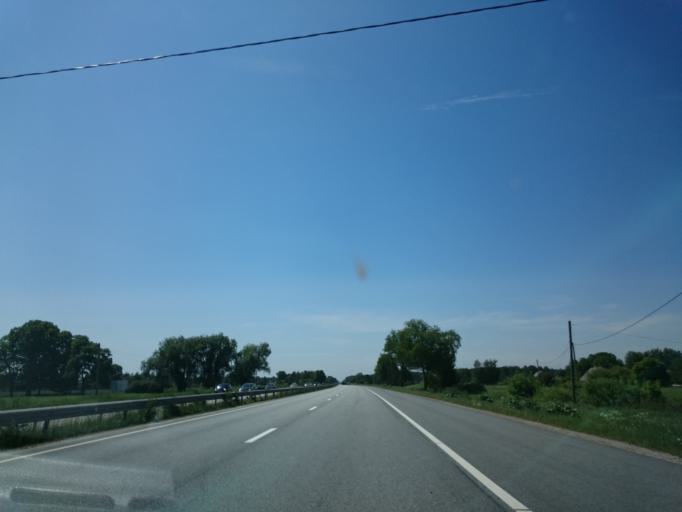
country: LV
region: Olaine
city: Olaine
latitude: 56.7746
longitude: 23.9316
